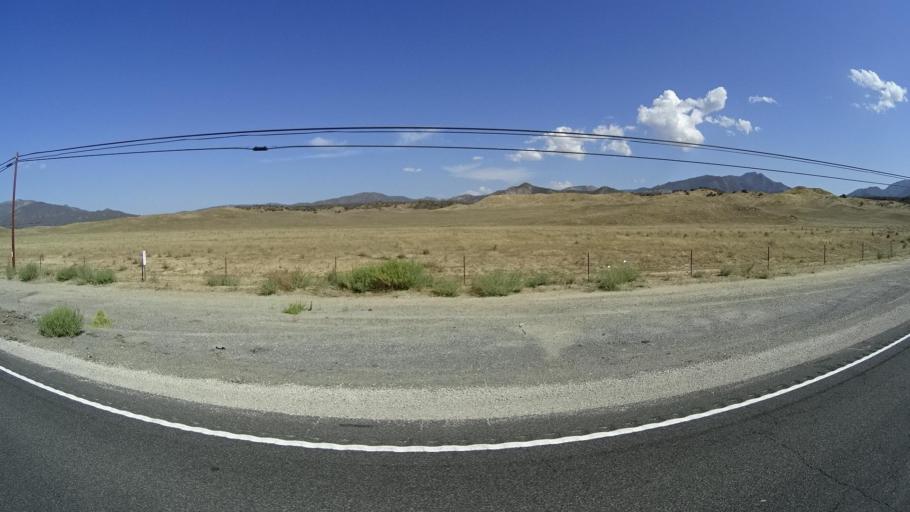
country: US
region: California
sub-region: San Diego County
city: Julian
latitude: 33.2850
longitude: -116.6715
